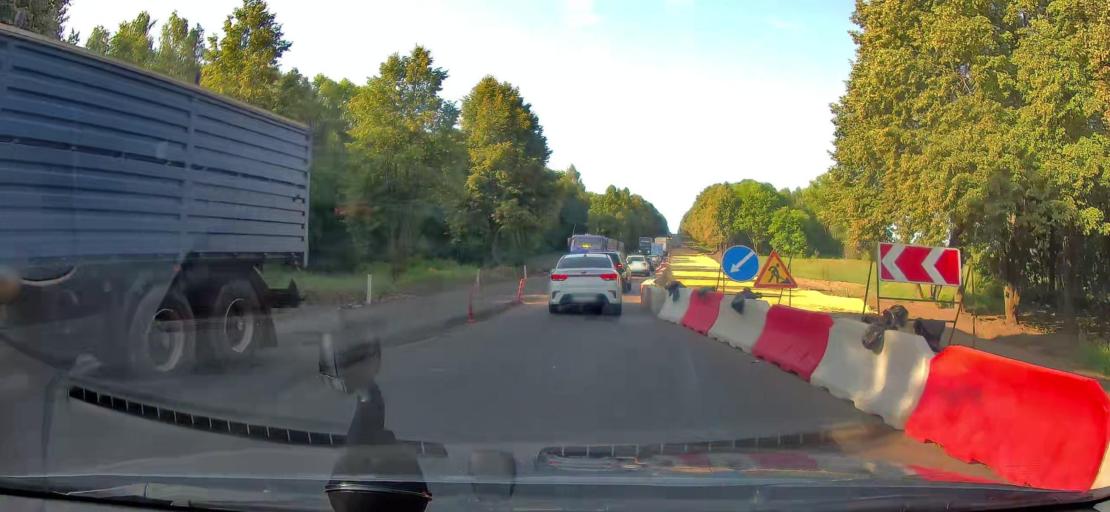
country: RU
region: Orjol
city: Spasskoye-Lutovinovo
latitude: 53.3675
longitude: 36.7298
